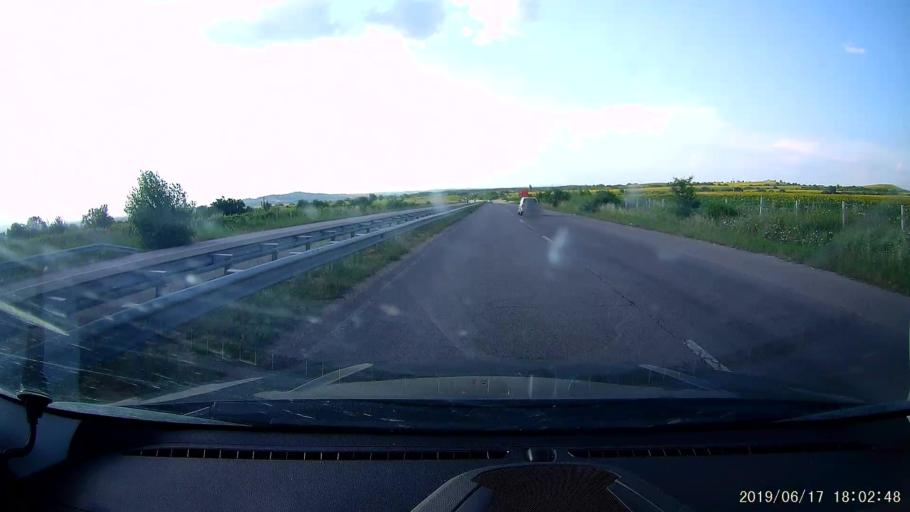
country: BG
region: Khaskovo
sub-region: Obshtina Svilengrad
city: Svilengrad
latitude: 41.7664
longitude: 26.2266
